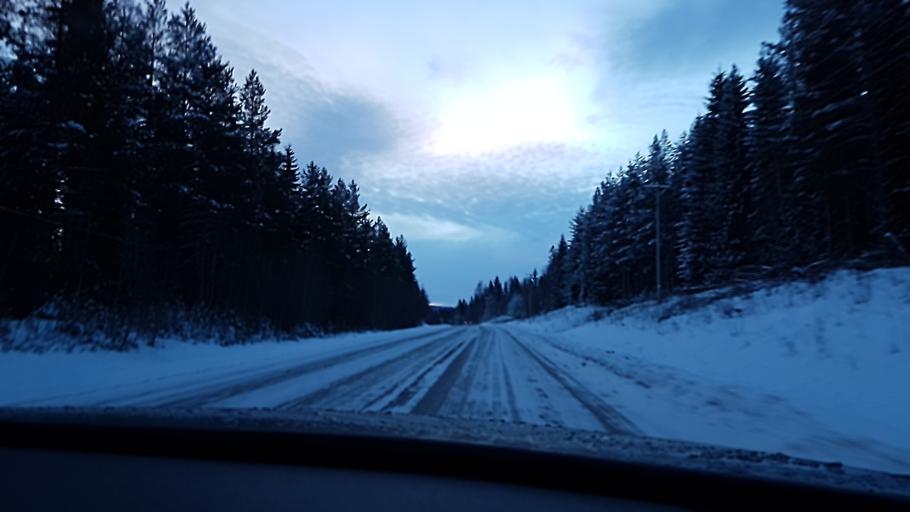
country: SE
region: Jaemtland
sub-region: Harjedalens Kommun
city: Sveg
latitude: 62.0794
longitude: 14.9454
